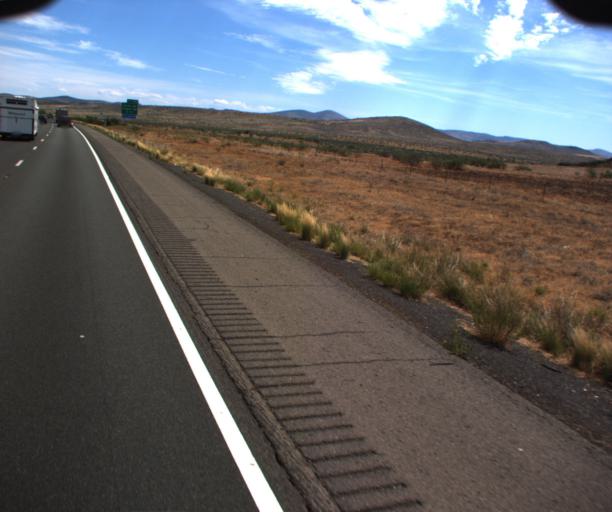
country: US
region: Arizona
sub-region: Yavapai County
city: Cordes Lakes
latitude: 34.3906
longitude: -112.0836
